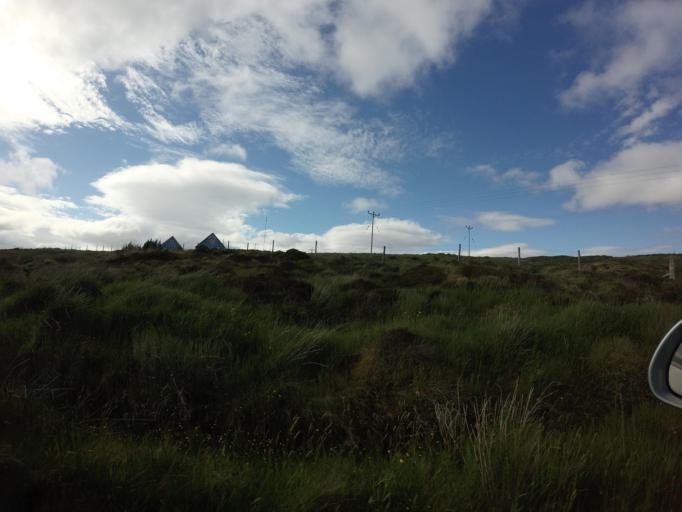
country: GB
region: Scotland
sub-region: Eilean Siar
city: Stornoway
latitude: 58.1719
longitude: -6.5725
